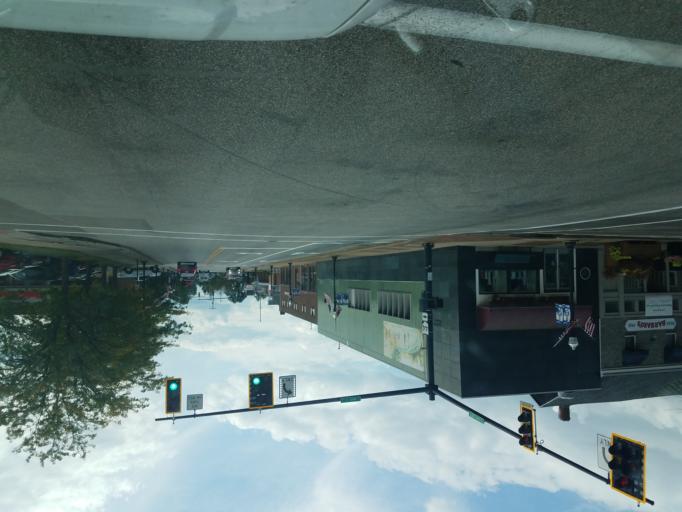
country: US
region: Ohio
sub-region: Stark County
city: Louisville
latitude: 40.8377
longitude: -81.2597
